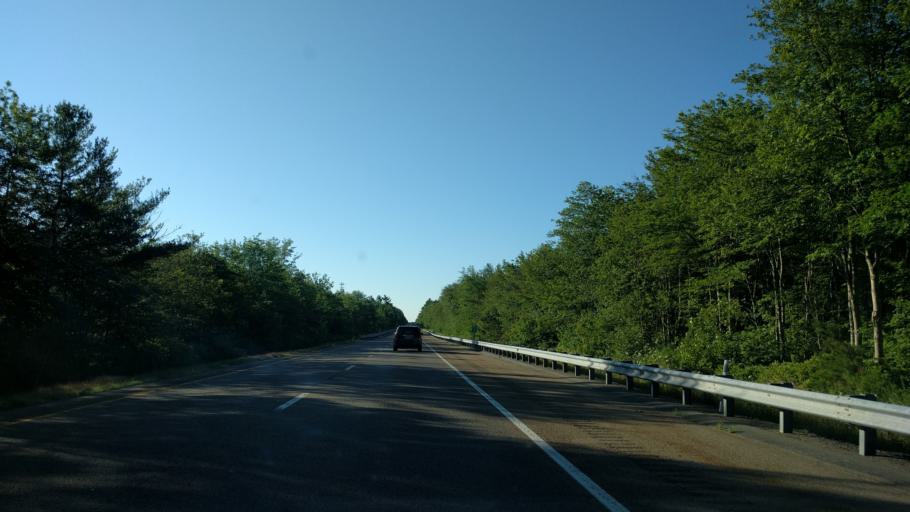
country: US
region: Massachusetts
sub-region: Plymouth County
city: West Wareham
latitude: 41.8324
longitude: -70.8185
